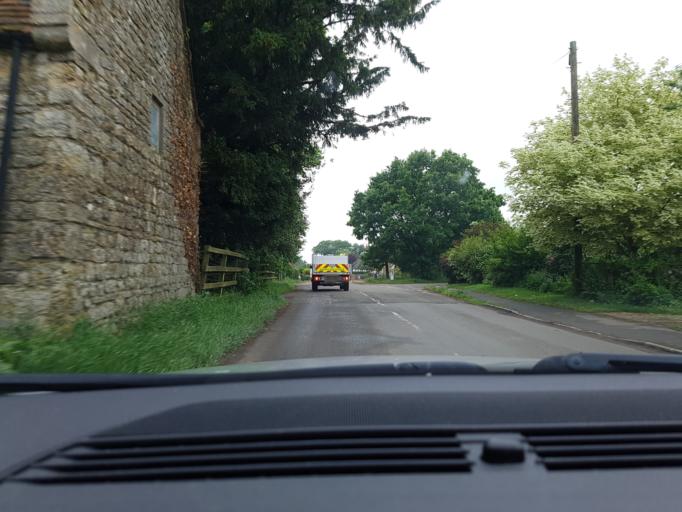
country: GB
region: England
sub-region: Buckinghamshire
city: Steeple Claydon
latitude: 51.9357
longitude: -0.9778
